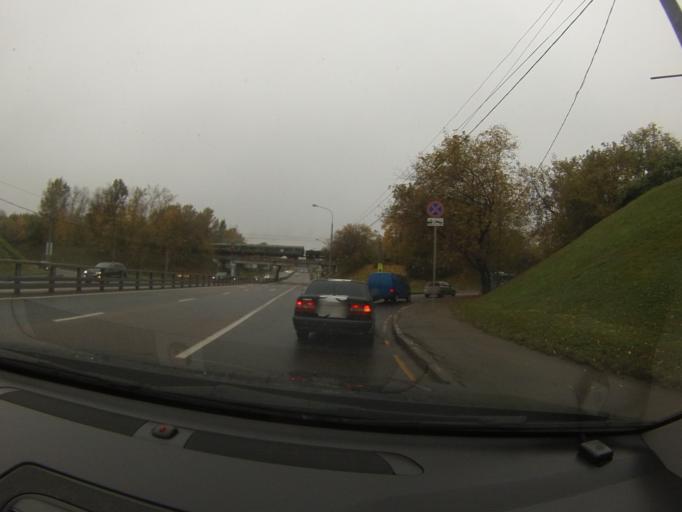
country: RU
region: Moskovskaya
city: Kastanayevo
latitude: 55.7320
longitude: 37.4903
